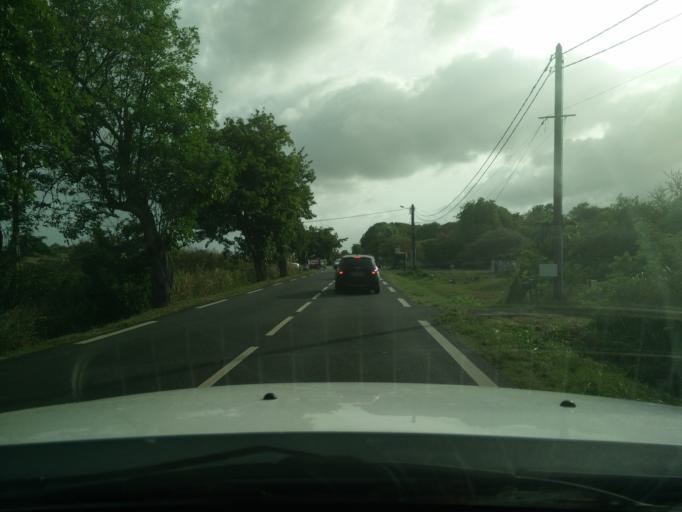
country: GP
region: Guadeloupe
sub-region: Guadeloupe
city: Saint-Francois
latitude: 16.2550
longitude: -61.3152
